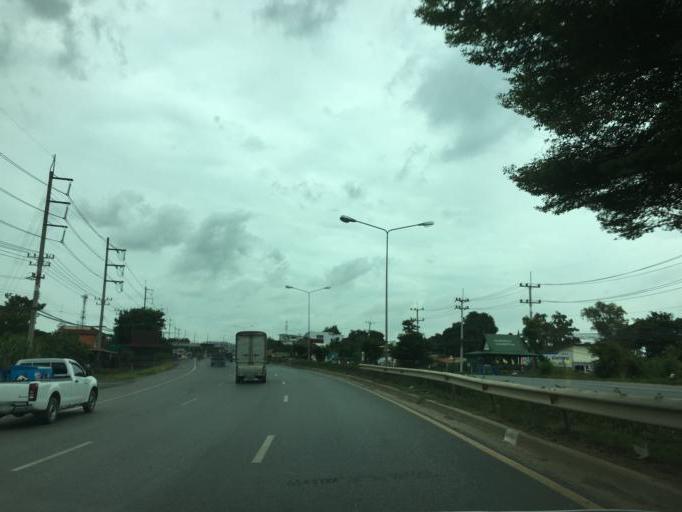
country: TH
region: Phra Nakhon Si Ayutthaya
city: Wang Noi
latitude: 14.2786
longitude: 100.6790
